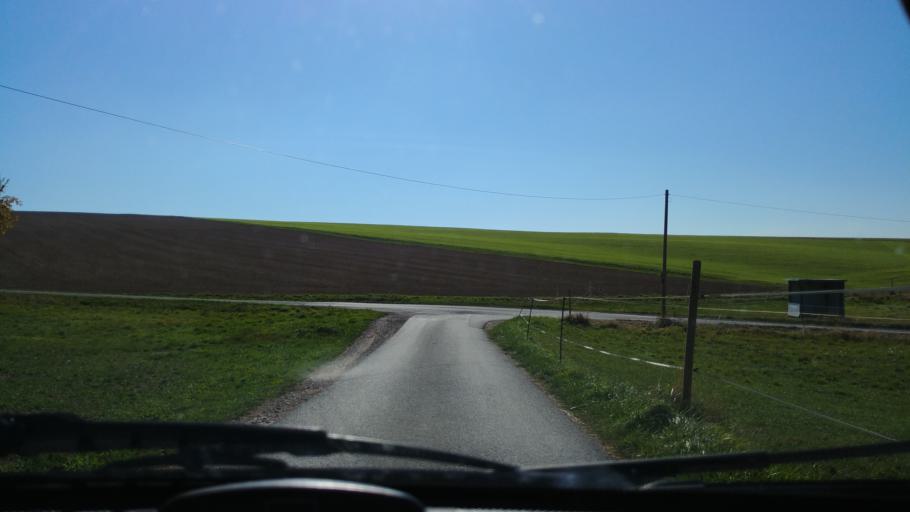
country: DE
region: Rheinland-Pfalz
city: Kaltenholzhausen
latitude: 50.2518
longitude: 8.1370
